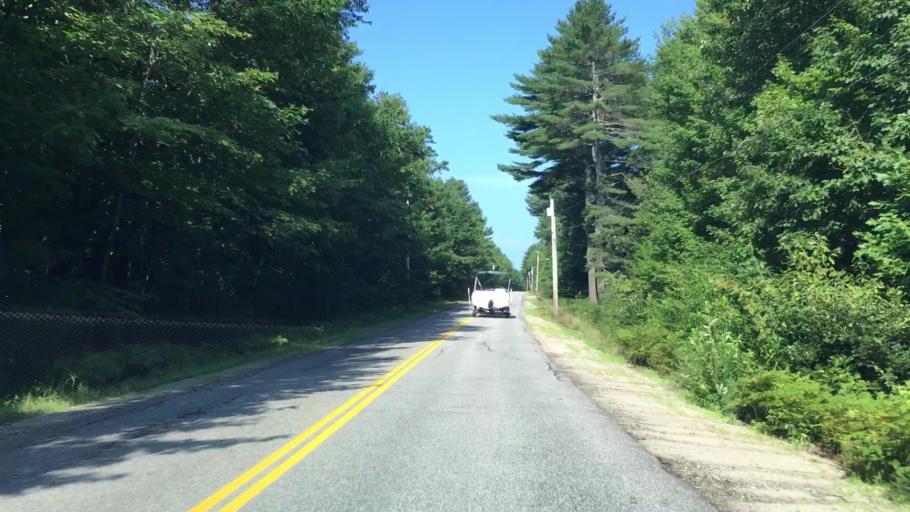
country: US
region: Maine
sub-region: Androscoggin County
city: Minot
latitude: 44.0427
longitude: -70.3425
